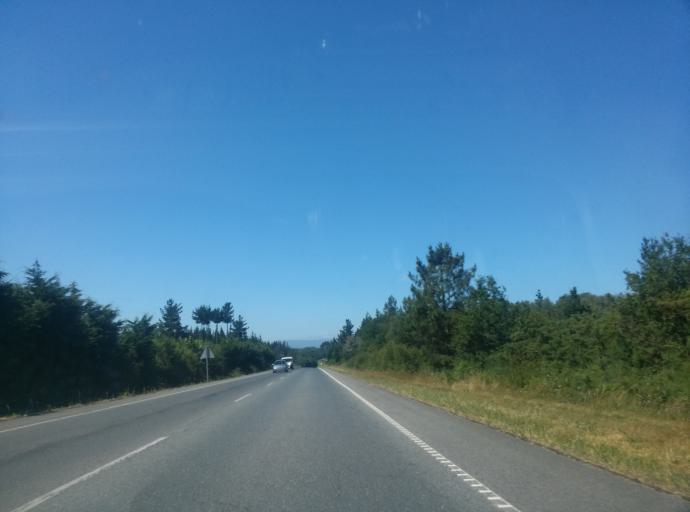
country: ES
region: Galicia
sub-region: Provincia de Lugo
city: Mos
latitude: 43.1127
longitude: -7.4841
